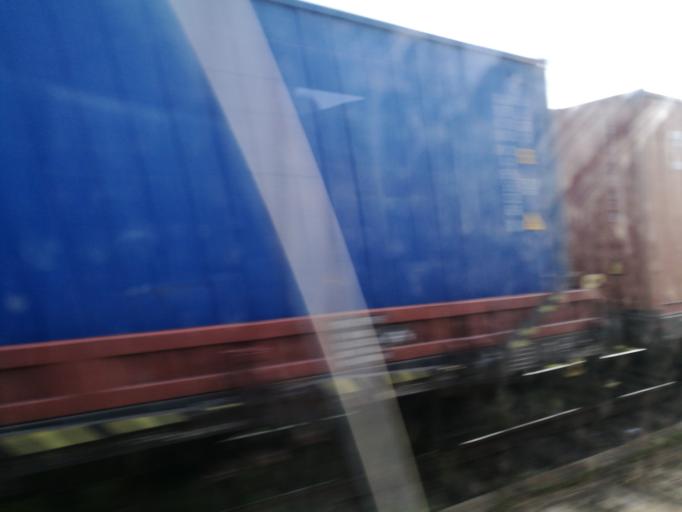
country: RO
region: Arges
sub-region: Comuna Leordeni
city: Leordeni
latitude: 44.7833
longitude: 25.1246
